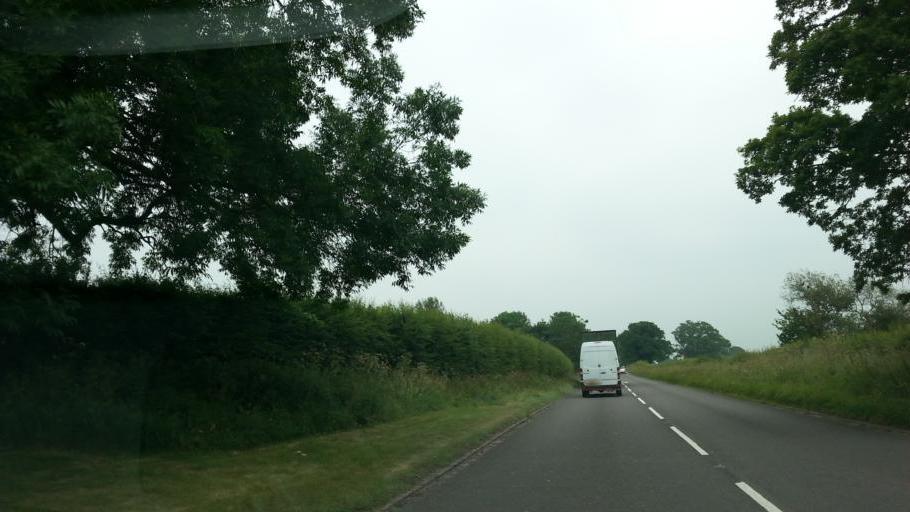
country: GB
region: England
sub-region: Staffordshire
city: Colwich
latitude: 52.8466
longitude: -2.0254
